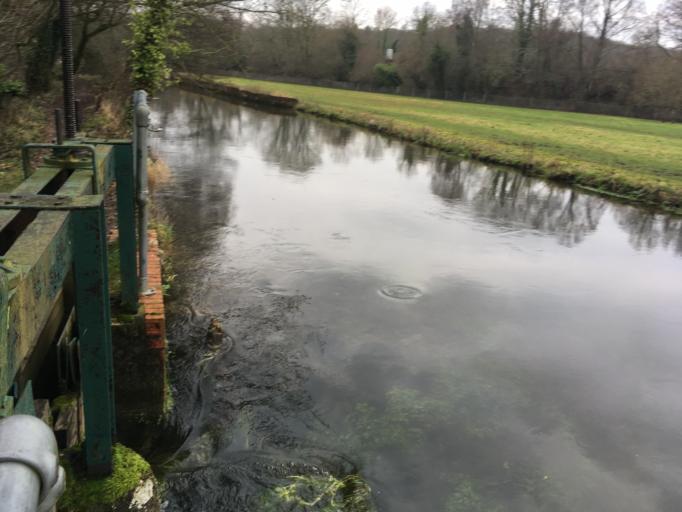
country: GB
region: England
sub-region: Hampshire
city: Compton
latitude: 50.9954
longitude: -1.3384
